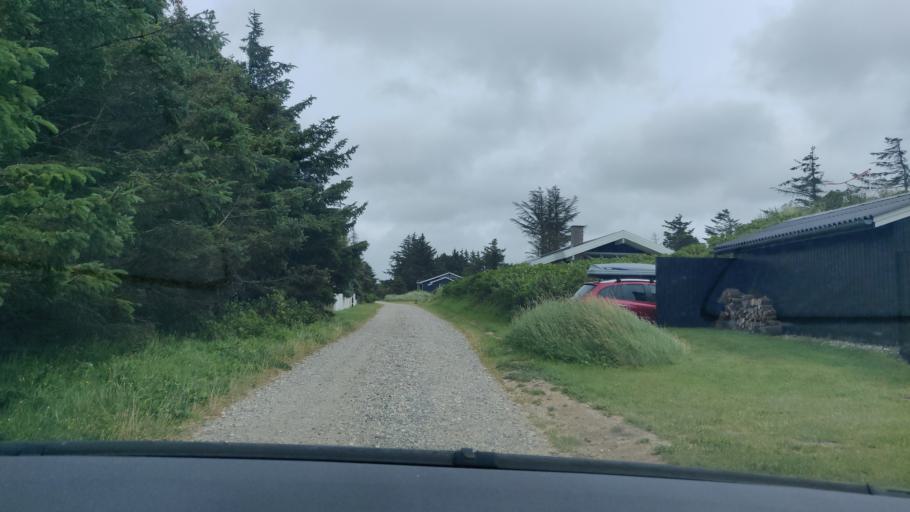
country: DK
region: North Denmark
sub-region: Jammerbugt Kommune
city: Pandrup
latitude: 57.2576
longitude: 9.5986
